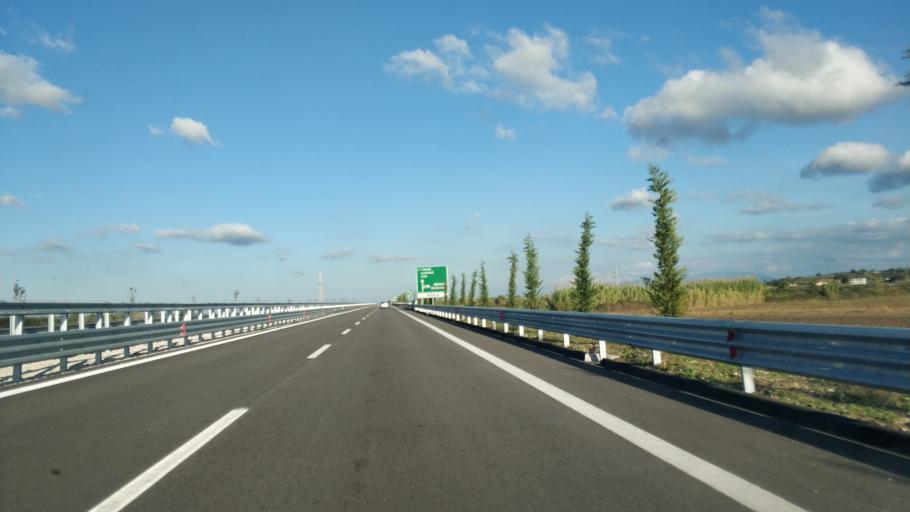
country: AL
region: Fier
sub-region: Rrethi i Fierit
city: Dermenas
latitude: 40.7393
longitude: 19.4646
